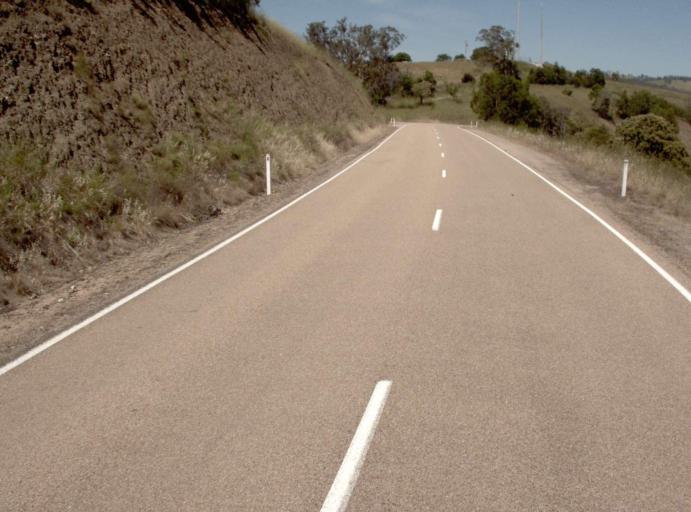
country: AU
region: Victoria
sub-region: East Gippsland
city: Lakes Entrance
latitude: -37.4915
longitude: 148.1851
